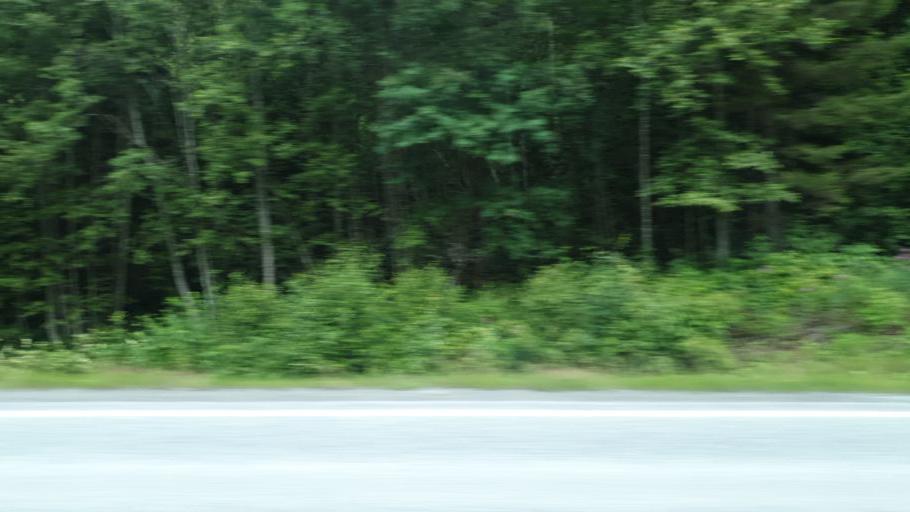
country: NO
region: Sor-Trondelag
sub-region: Midtre Gauldal
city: Storen
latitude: 63.0114
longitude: 10.2455
